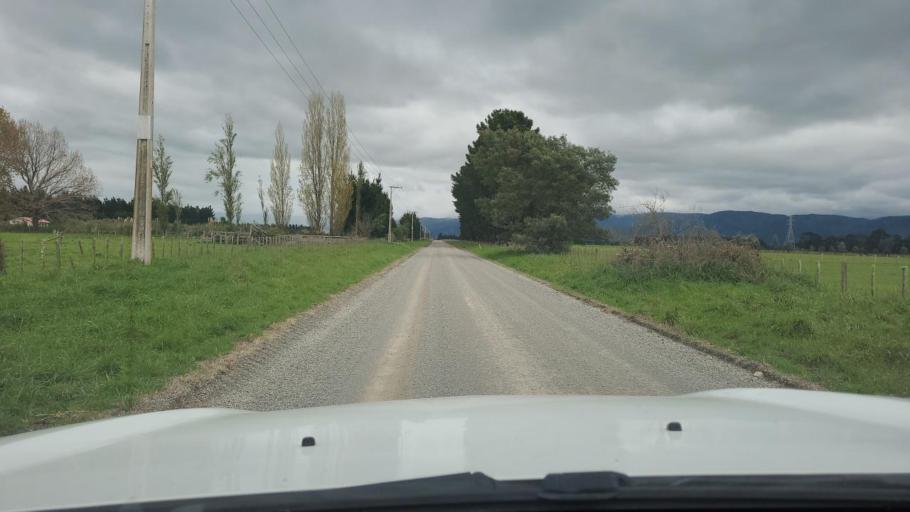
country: NZ
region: Wellington
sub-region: Masterton District
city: Masterton
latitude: -41.1189
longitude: 175.4151
